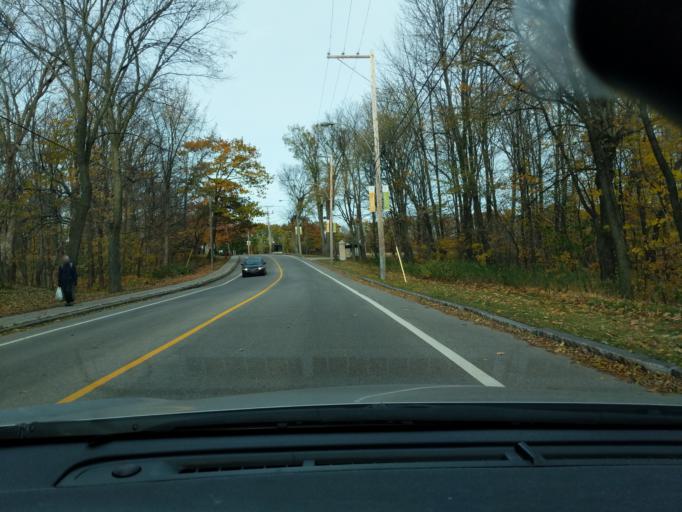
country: CA
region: Quebec
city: Quebec
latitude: 46.7744
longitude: -71.2549
